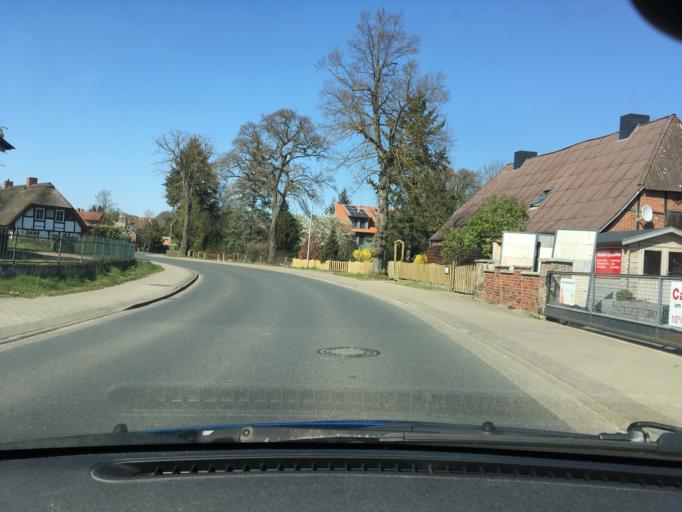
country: DE
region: Lower Saxony
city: Hitzacker
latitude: 53.1435
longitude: 11.0422
